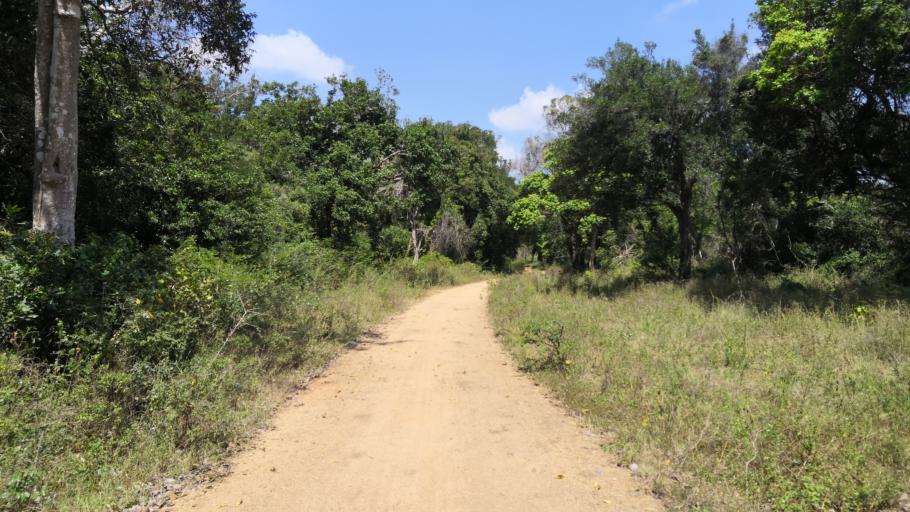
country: LK
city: Padaviya Divisional Secretariat
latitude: 8.9639
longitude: 80.6904
